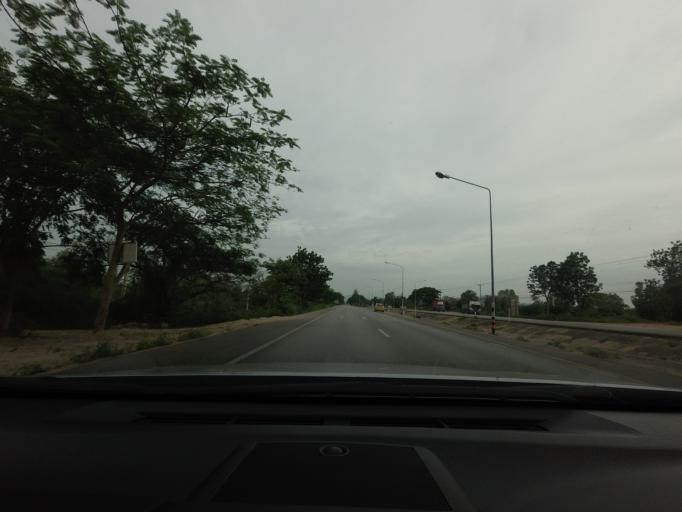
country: TH
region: Phetchaburi
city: Cha-am
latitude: 12.7530
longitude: 99.9320
